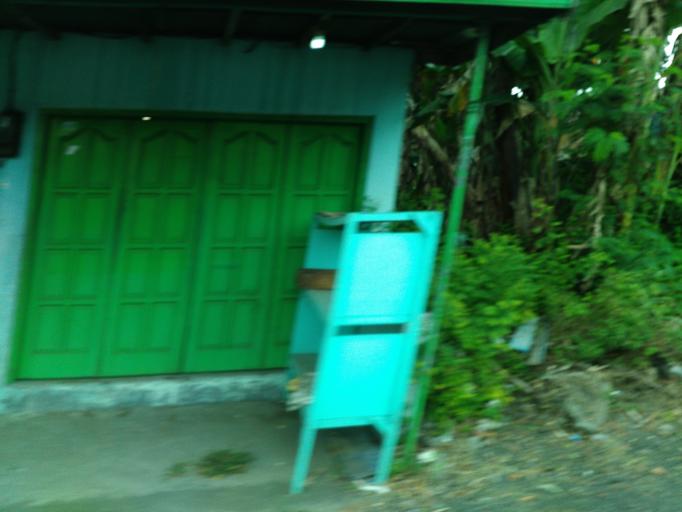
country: ID
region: Central Java
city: Ceper
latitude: -7.6519
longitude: 110.6829
